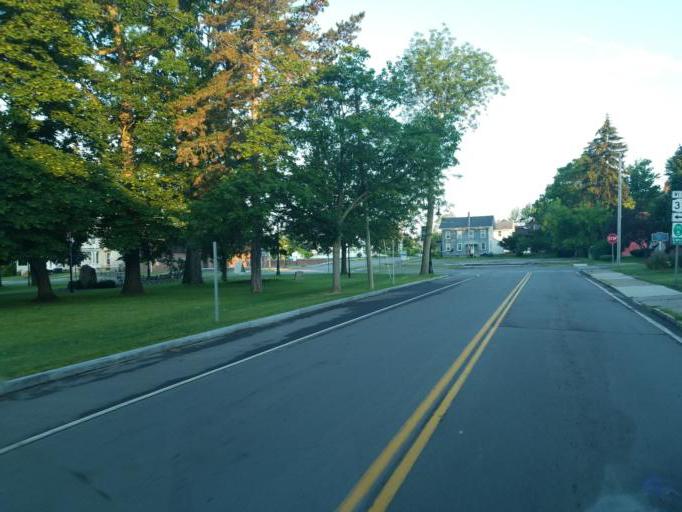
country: US
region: New York
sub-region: Wayne County
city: Clyde
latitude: 43.0844
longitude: -76.8704
